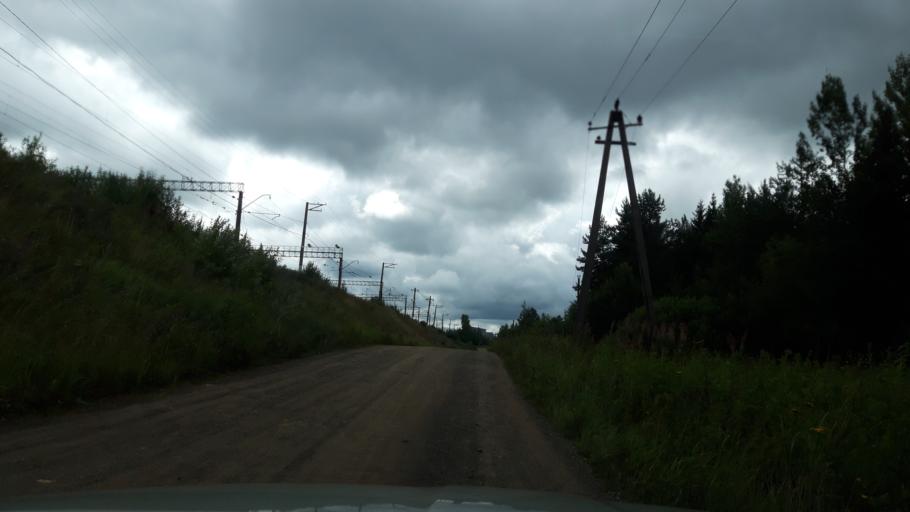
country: RU
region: Moskovskaya
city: Povarovo
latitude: 56.0511
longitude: 37.0570
